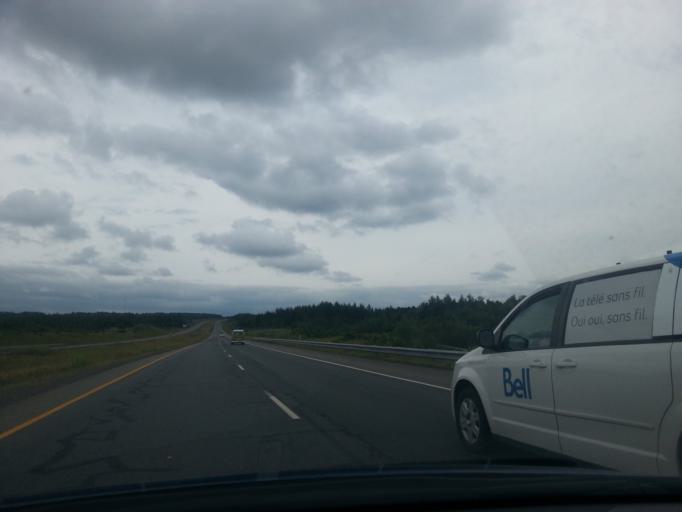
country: US
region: Maine
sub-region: Aroostook County
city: Madawaska
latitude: 47.3279
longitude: -68.1256
